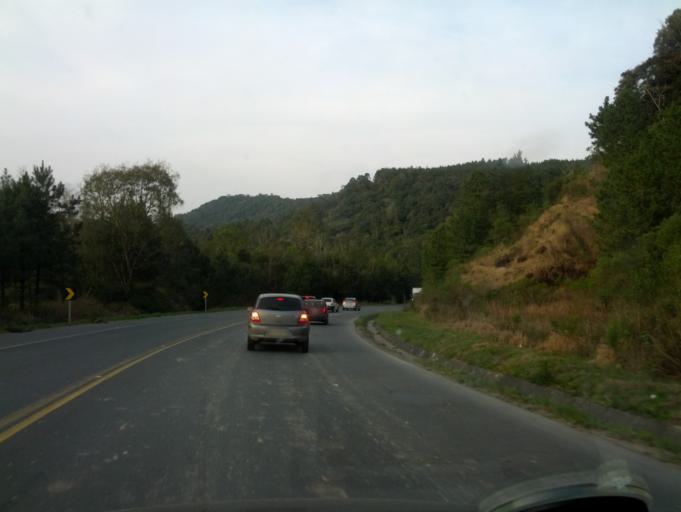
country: BR
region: Santa Catarina
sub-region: Otacilio Costa
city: Otacilio Costa
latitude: -27.2814
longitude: -50.0696
